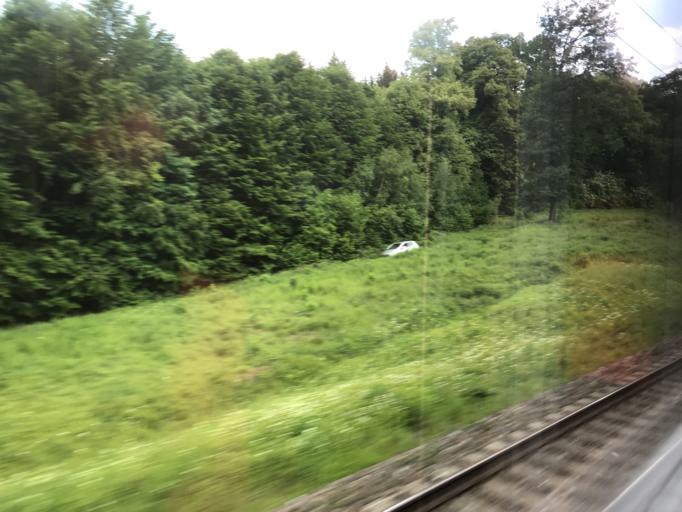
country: DE
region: Bavaria
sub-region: Swabia
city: Rosshaupten
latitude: 48.3945
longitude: 10.4747
